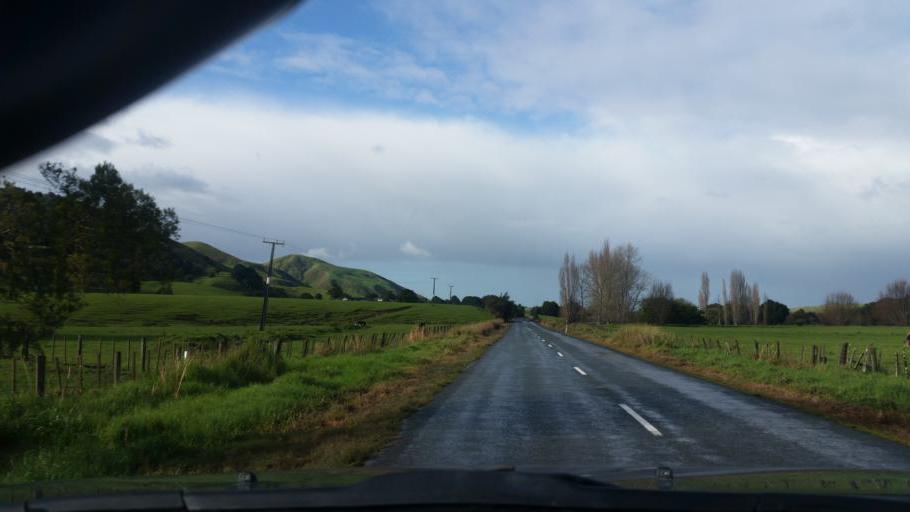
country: NZ
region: Northland
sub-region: Kaipara District
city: Dargaville
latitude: -35.8040
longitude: 173.9200
